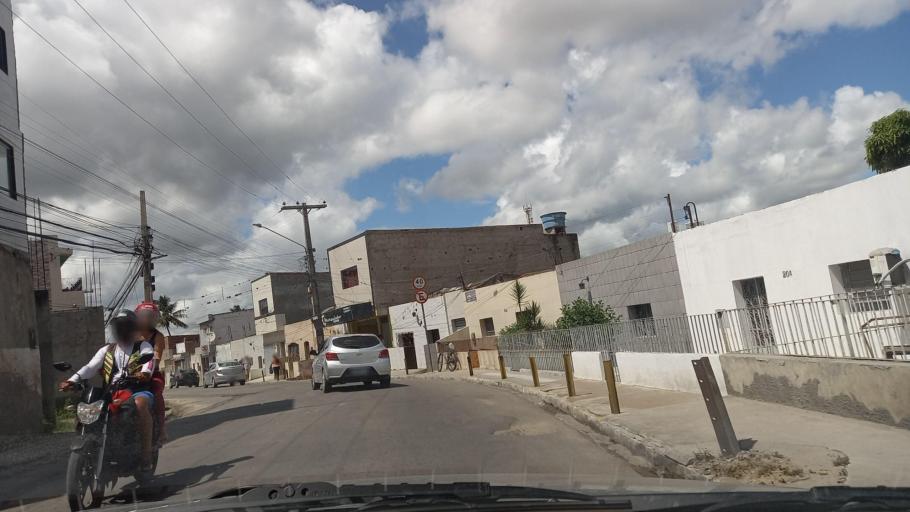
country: BR
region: Pernambuco
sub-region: Caruaru
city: Caruaru
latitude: -8.2830
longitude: -35.9615
